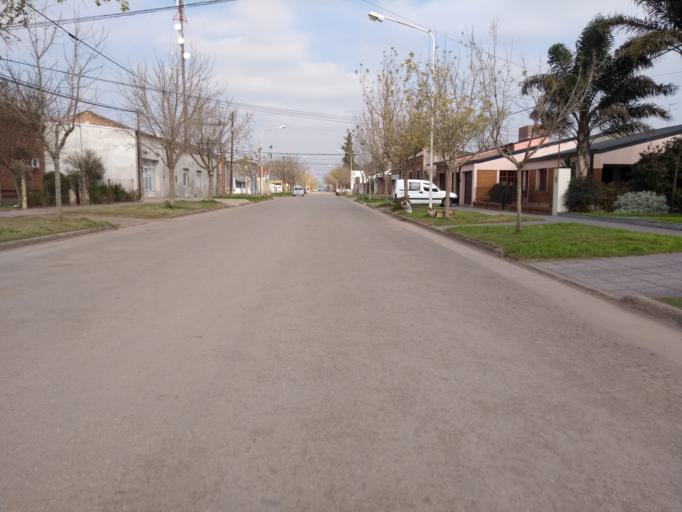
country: AR
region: Santa Fe
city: Galvez
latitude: -31.9027
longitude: -61.2780
